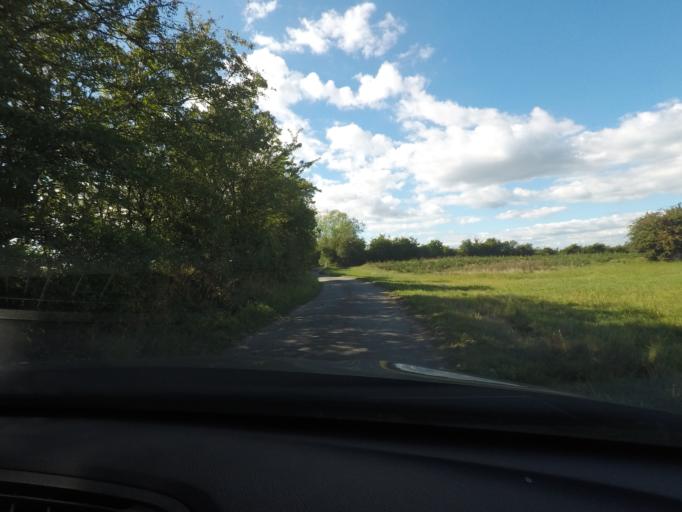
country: DK
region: Zealand
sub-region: Guldborgsund Kommune
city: Sakskobing
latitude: 54.9683
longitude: 11.5493
